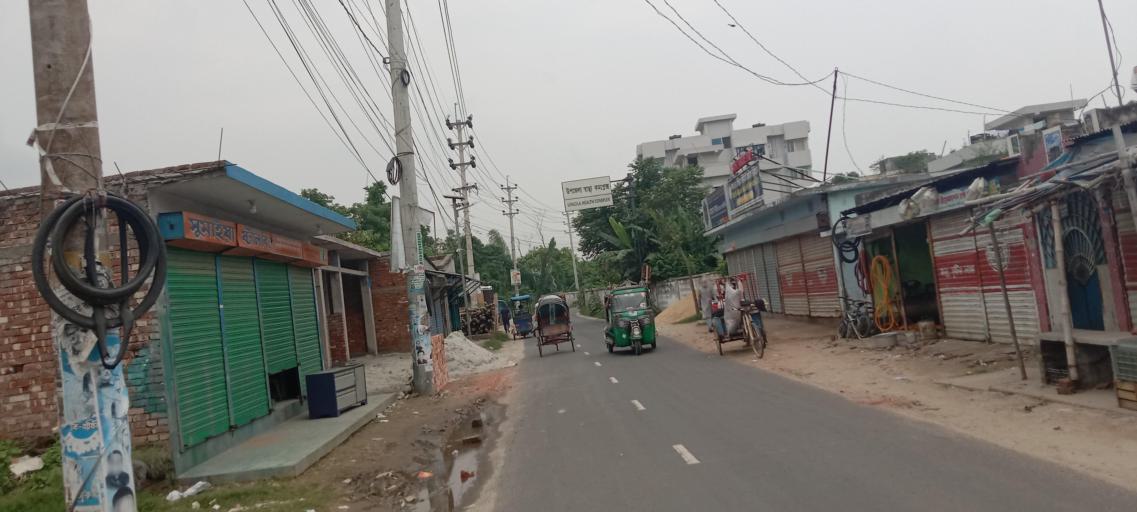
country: BD
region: Dhaka
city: Azimpur
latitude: 23.7083
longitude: 90.3475
